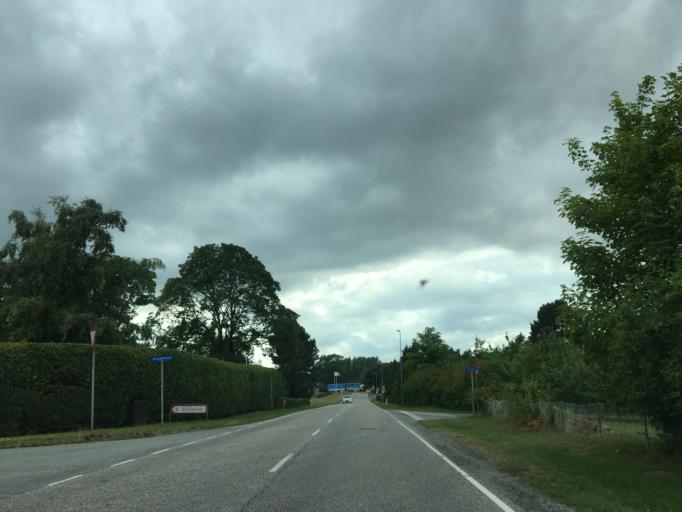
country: DK
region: South Denmark
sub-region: Middelfart Kommune
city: Ejby
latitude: 55.4025
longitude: 9.9854
